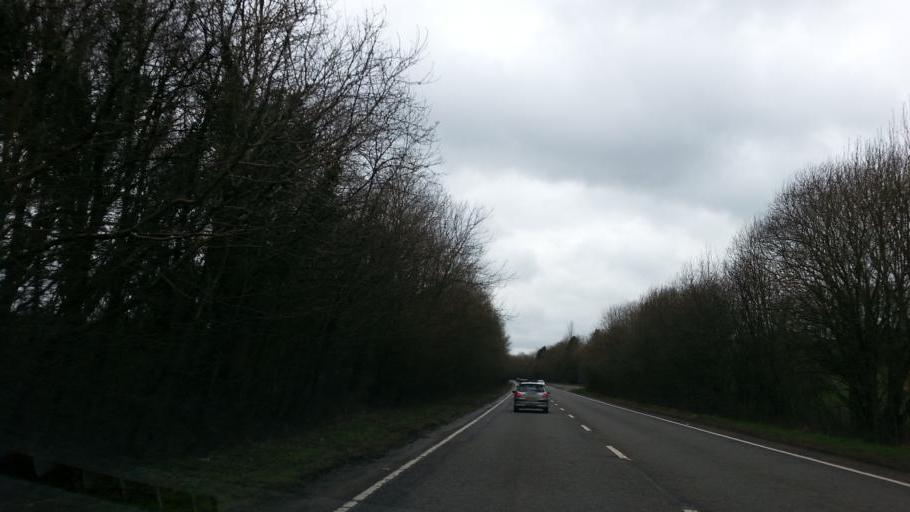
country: GB
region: England
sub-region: Devon
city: South Molton
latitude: 51.0483
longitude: -3.8970
